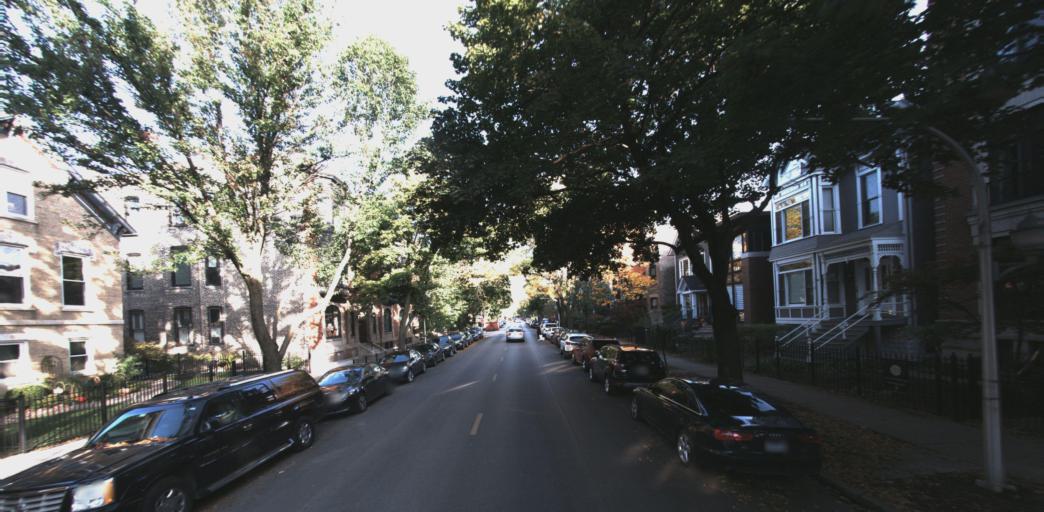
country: US
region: Illinois
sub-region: Cook County
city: Chicago
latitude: 41.9290
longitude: -87.6510
